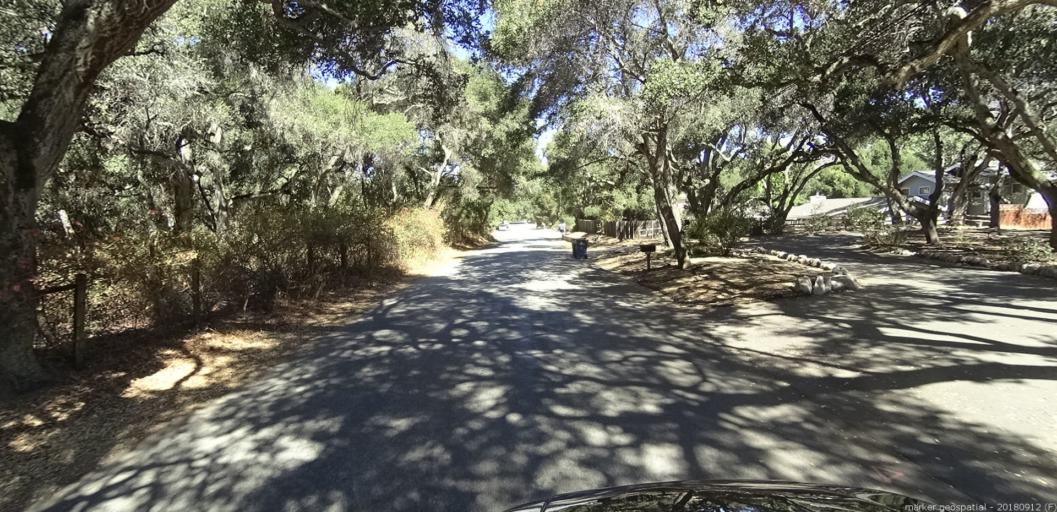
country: US
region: California
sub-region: Monterey County
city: Carmel Valley Village
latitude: 36.4877
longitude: -121.7489
